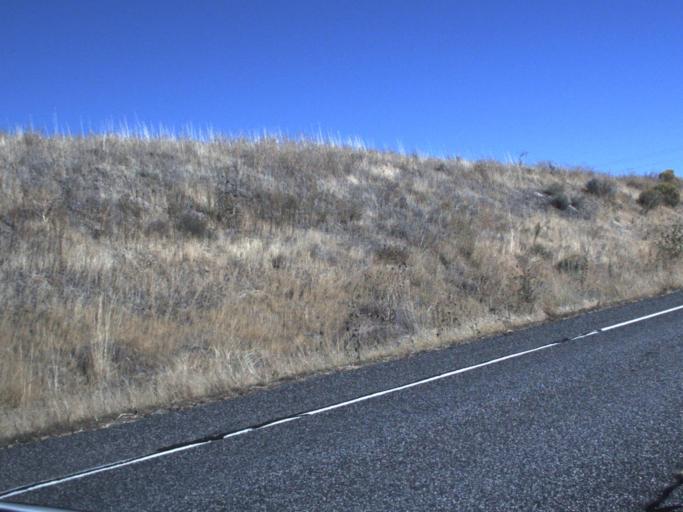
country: US
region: Washington
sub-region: Walla Walla County
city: Burbank
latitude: 46.2978
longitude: -118.7144
